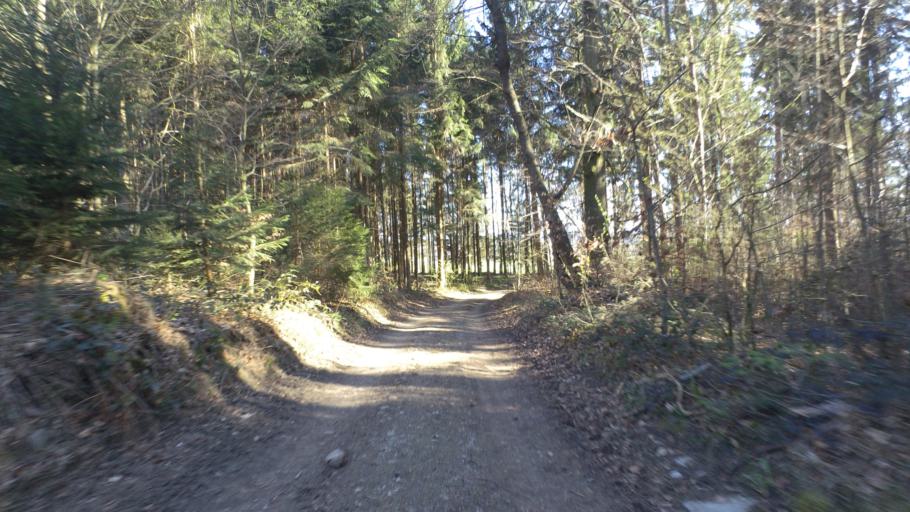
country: DE
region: Bavaria
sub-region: Upper Bavaria
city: Chieming
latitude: 47.9438
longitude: 12.5218
